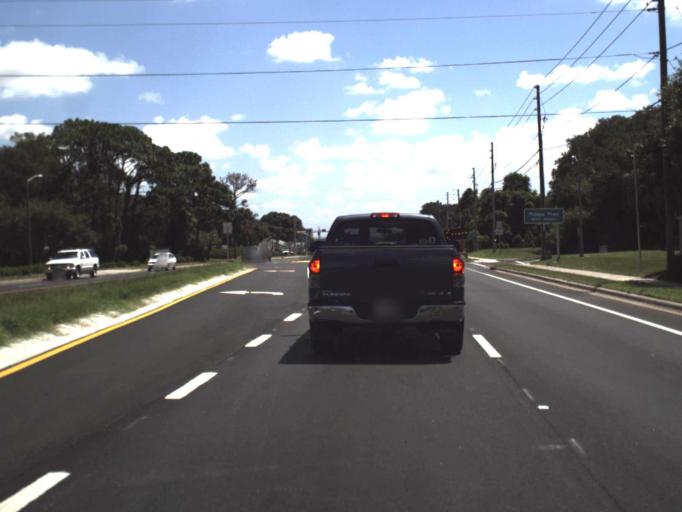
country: US
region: Florida
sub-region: Pinellas County
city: Oldsmar
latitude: 28.0269
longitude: -82.6979
